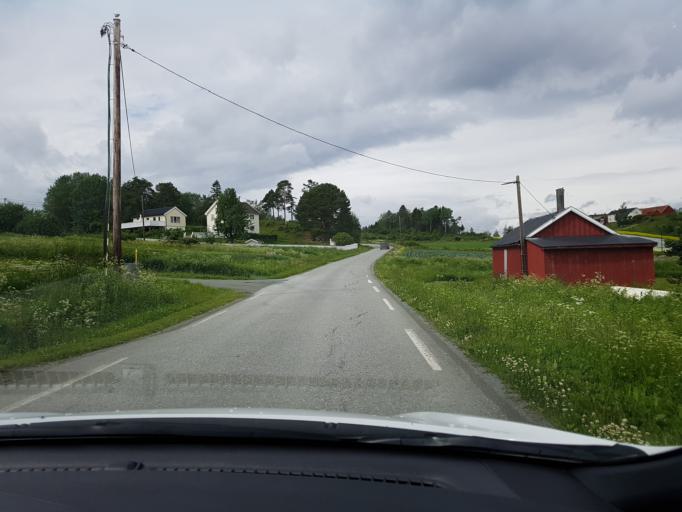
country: NO
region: Nord-Trondelag
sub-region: Frosta
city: Frosta
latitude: 63.6319
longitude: 10.7844
